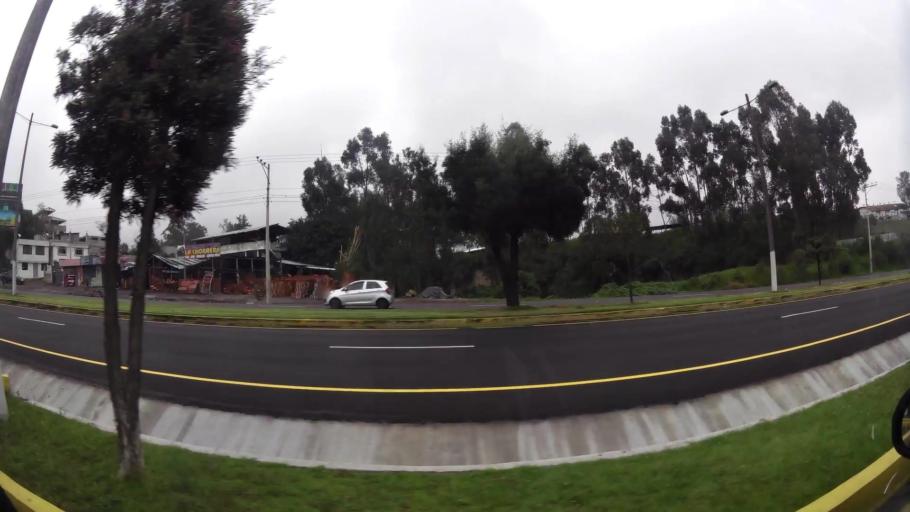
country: EC
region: Pichincha
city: Sangolqui
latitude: -0.2794
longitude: -78.4776
